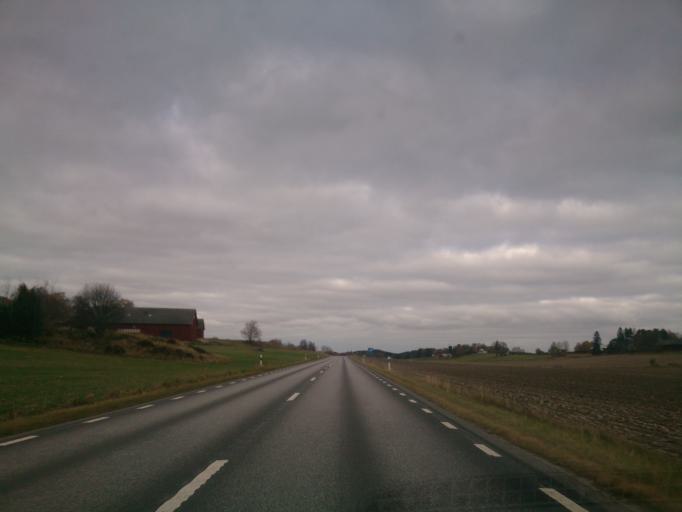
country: SE
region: OEstergoetland
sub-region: Linkopings Kommun
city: Sturefors
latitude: 58.3386
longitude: 15.8476
